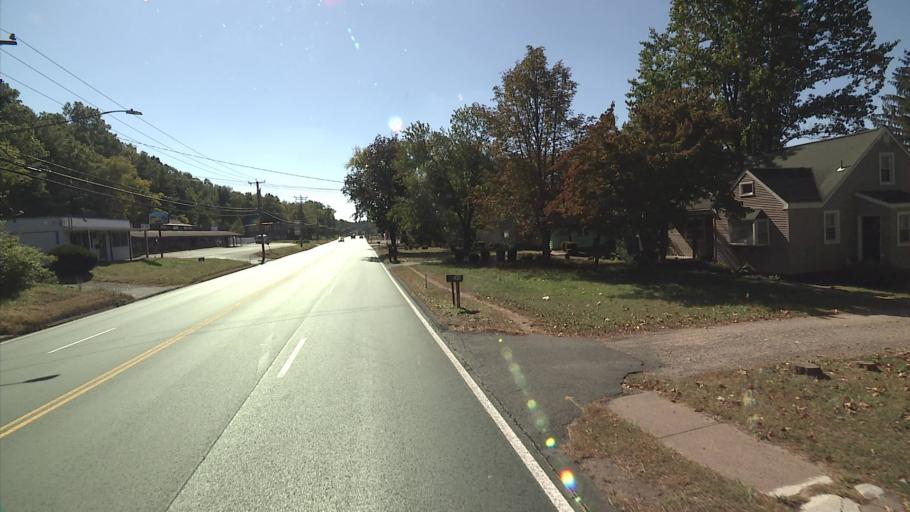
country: US
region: Connecticut
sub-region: Tolland County
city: Rockville
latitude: 41.8574
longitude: -72.4849
